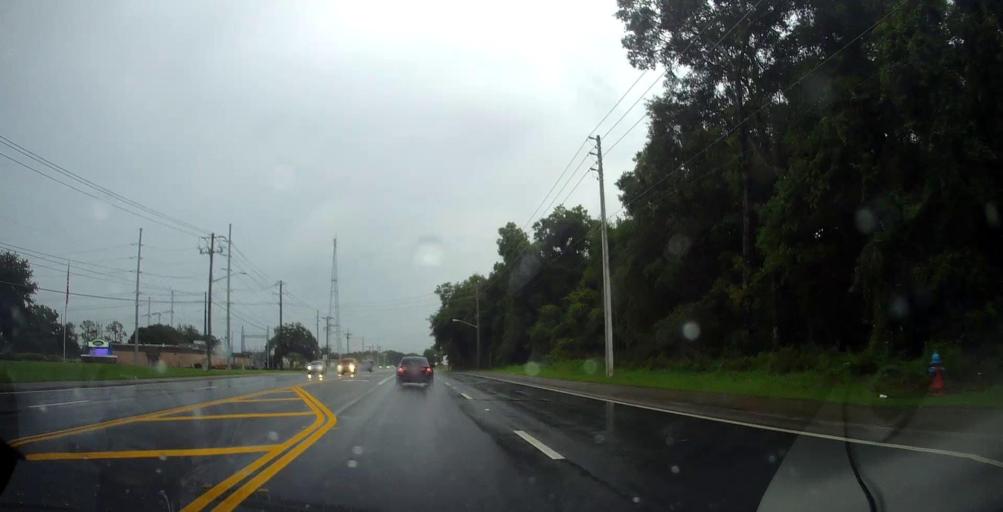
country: US
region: Florida
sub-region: Marion County
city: Ocala
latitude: 29.1627
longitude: -82.0869
